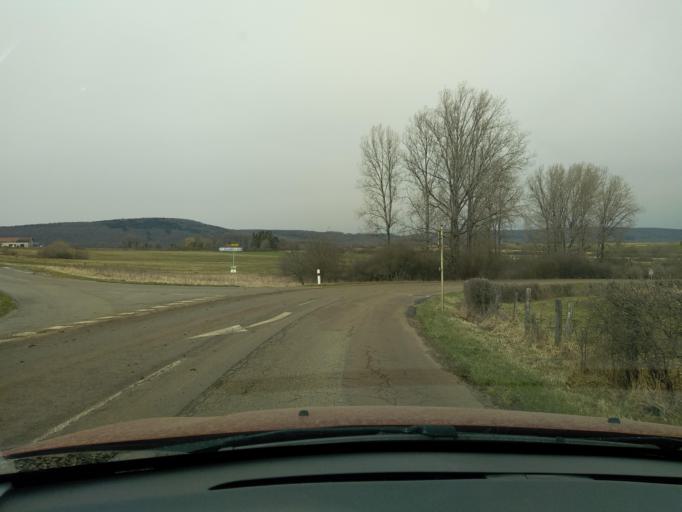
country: FR
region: Franche-Comte
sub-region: Departement du Jura
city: Clairvaux-les-Lacs
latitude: 46.6667
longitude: 5.7676
